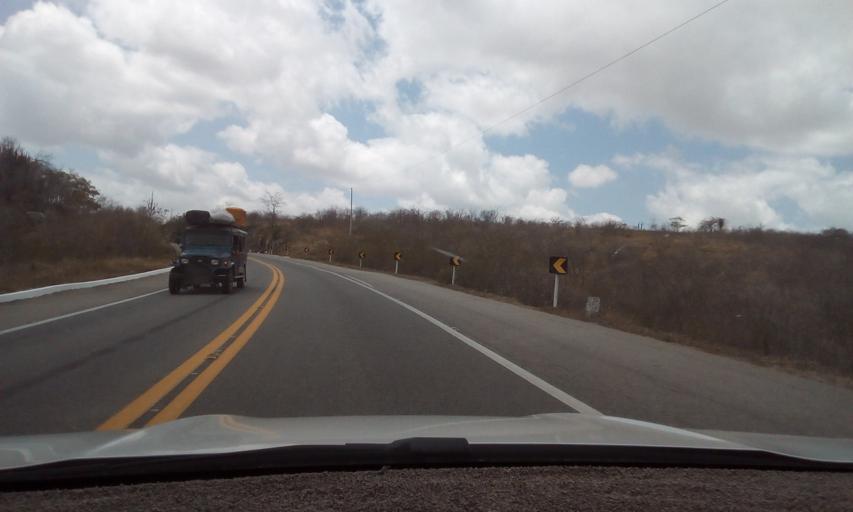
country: BR
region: Pernambuco
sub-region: Taquaritinga Do Norte
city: Taquaritinga do Norte
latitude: -7.6875
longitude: -36.0619
